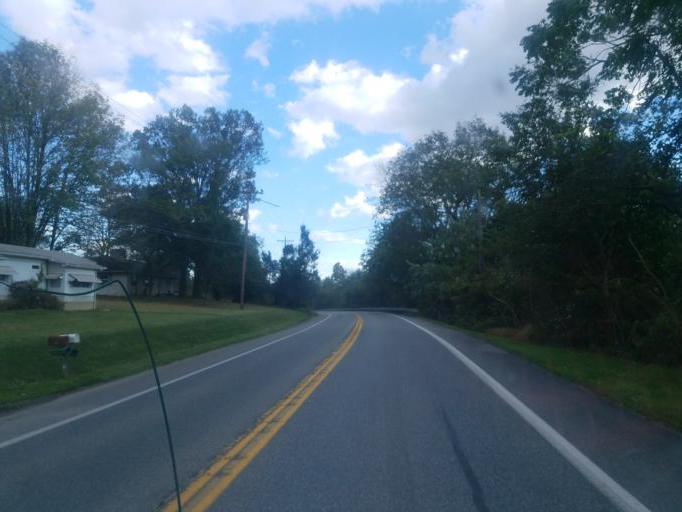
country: US
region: Pennsylvania
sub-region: Lancaster County
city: Bainbridge
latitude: 40.1206
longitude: -76.7079
